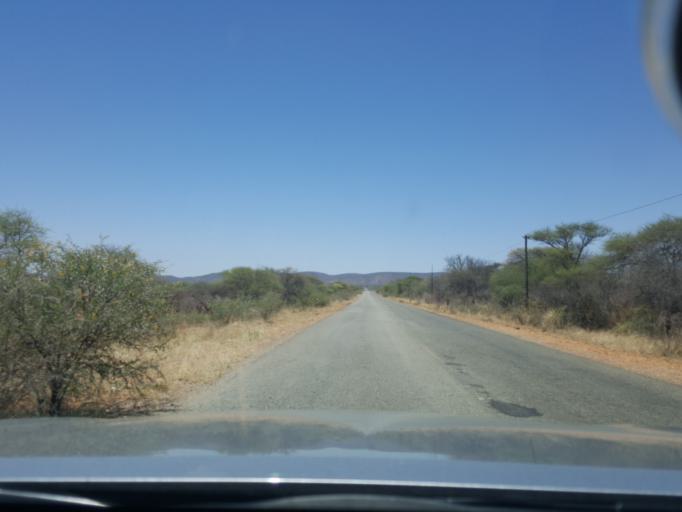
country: BW
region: South East
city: Lobatse
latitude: -25.2240
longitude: 25.9401
